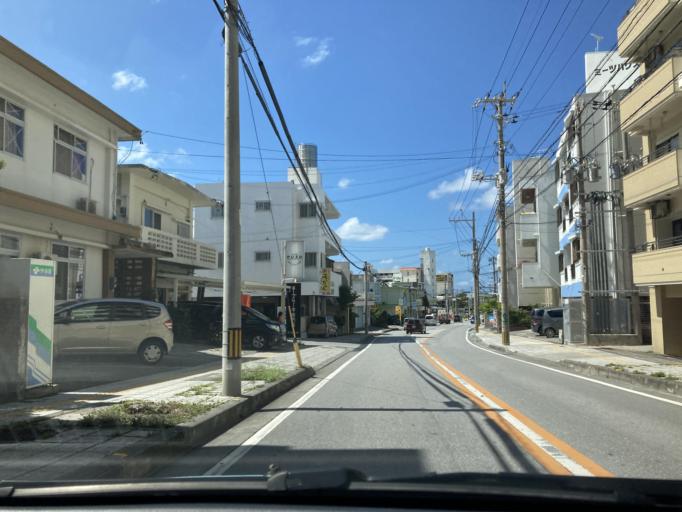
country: JP
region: Okinawa
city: Tomigusuku
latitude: 26.1932
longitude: 127.6635
